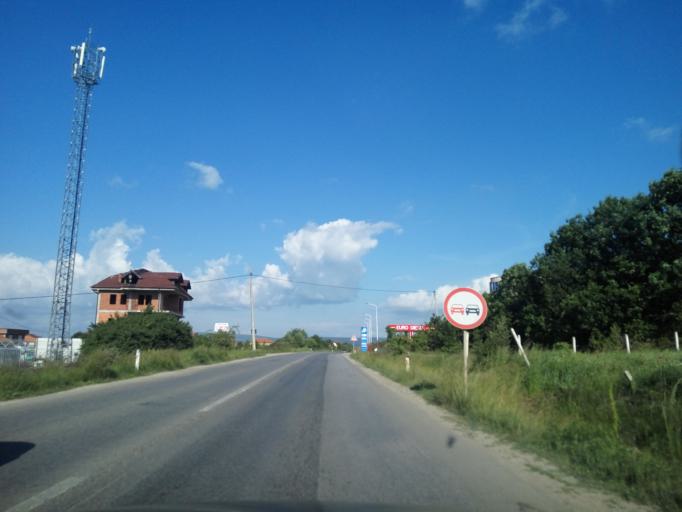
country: XK
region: Prizren
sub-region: Komuna e Malisheves
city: Llazice
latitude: 42.5871
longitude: 20.6809
